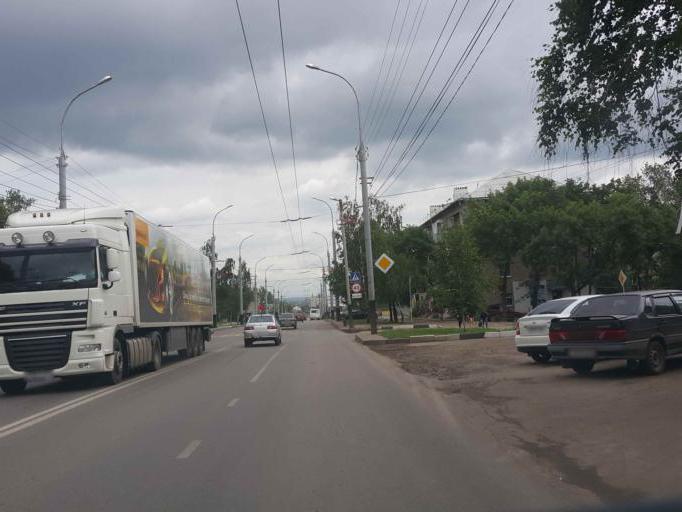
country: RU
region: Tambov
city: Tambov
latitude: 52.7448
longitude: 41.4248
